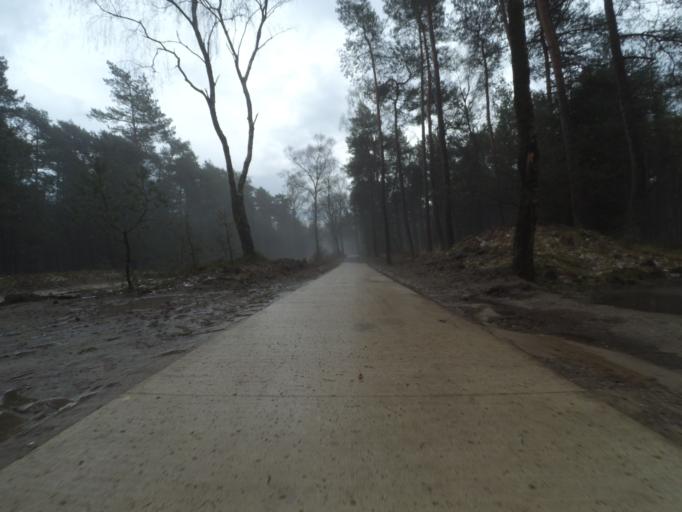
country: NL
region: Gelderland
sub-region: Gemeente Apeldoorn
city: Beekbergen
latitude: 52.1364
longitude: 5.9074
